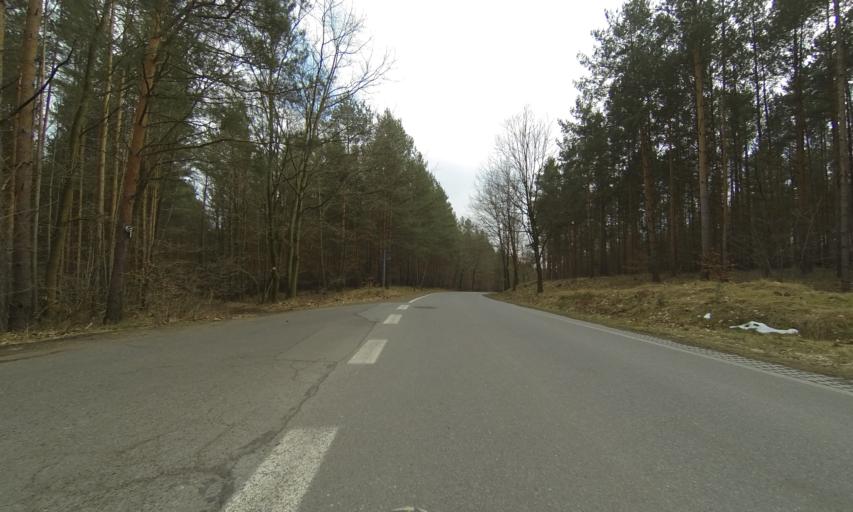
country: DE
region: Saxony
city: Radebeul
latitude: 51.1087
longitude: 13.7157
